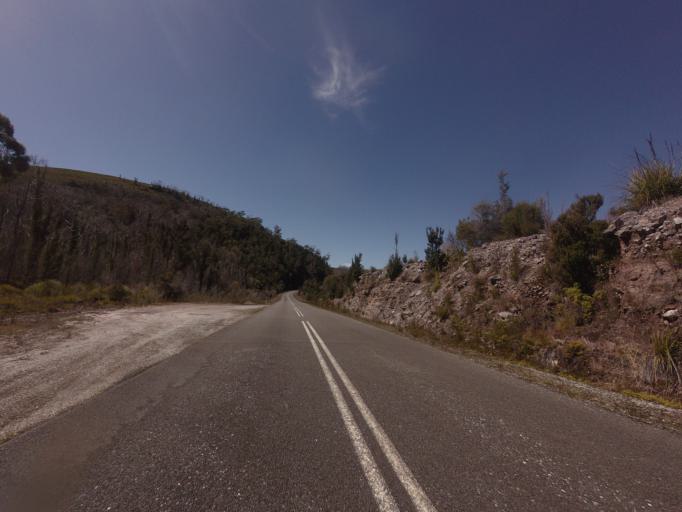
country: AU
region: Tasmania
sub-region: Huon Valley
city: Geeveston
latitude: -42.8597
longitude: 146.2288
